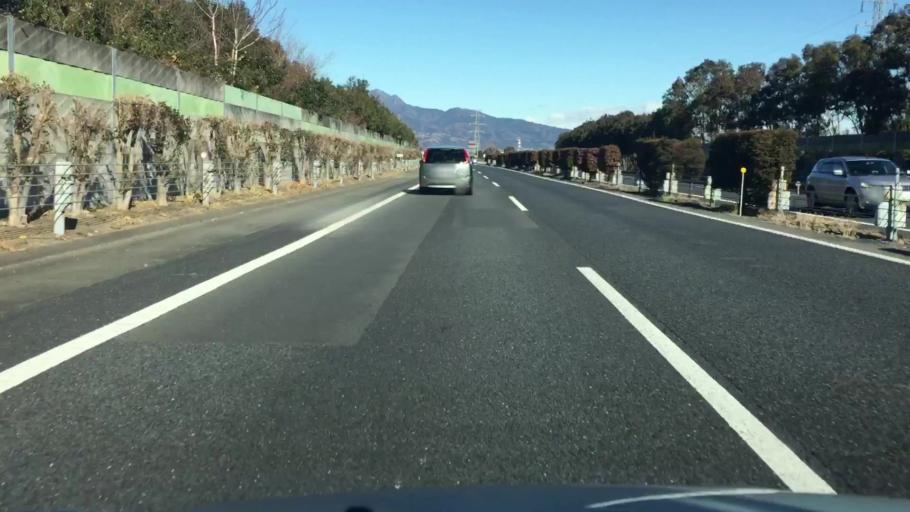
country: JP
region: Gunma
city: Shibukawa
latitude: 36.4471
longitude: 139.0149
